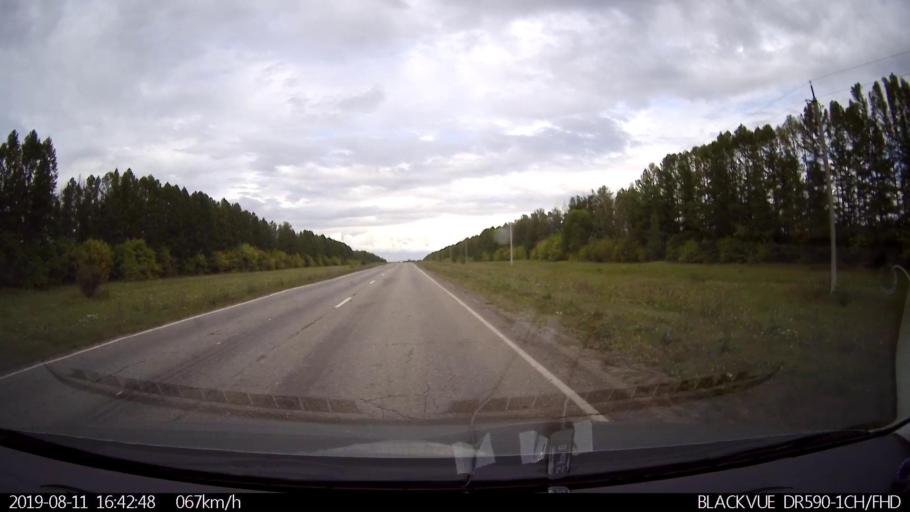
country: RU
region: Ulyanovsk
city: Mayna
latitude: 54.1636
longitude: 47.6659
